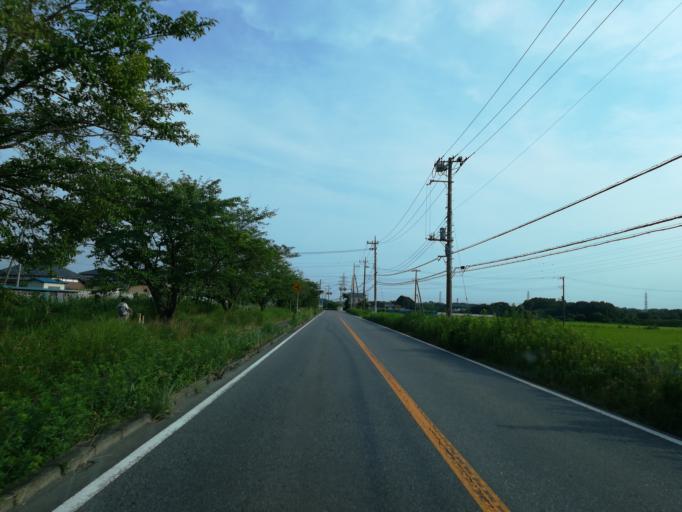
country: JP
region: Ibaraki
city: Tsukuba
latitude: 36.1849
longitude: 140.0790
